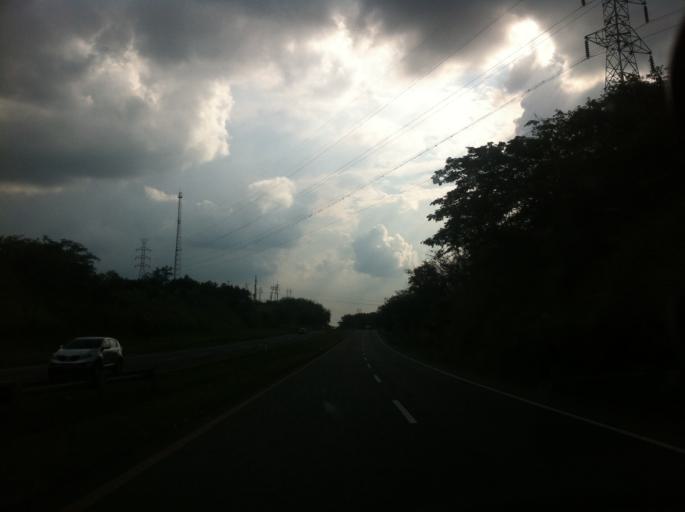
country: CO
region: Valle del Cauca
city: Tulua
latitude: 4.0833
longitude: -76.1732
